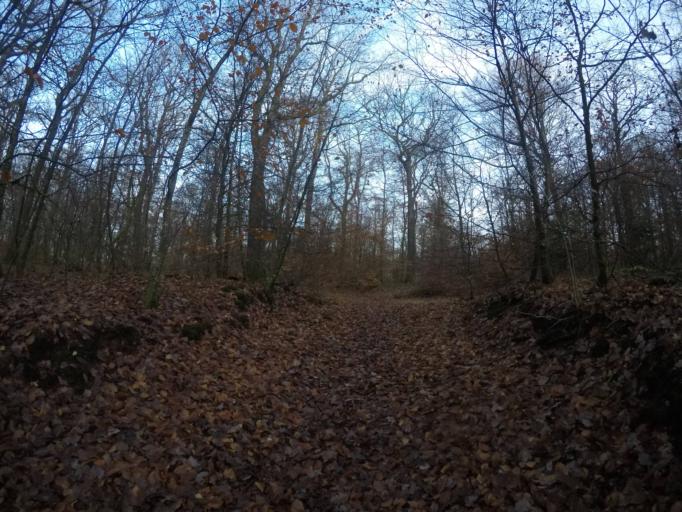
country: BE
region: Wallonia
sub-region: Province du Luxembourg
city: Habay-la-Vieille
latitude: 49.7449
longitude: 5.6733
